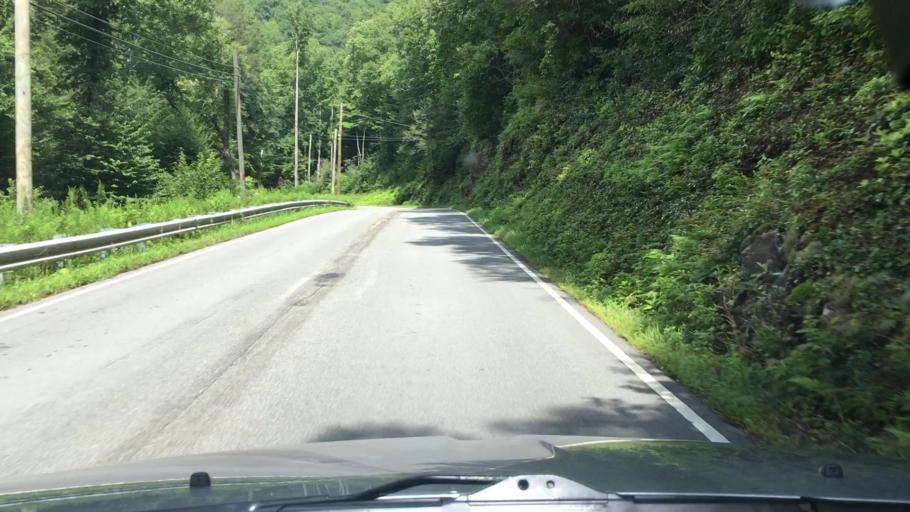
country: US
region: North Carolina
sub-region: Yancey County
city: Burnsville
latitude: 35.7814
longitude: -82.2036
